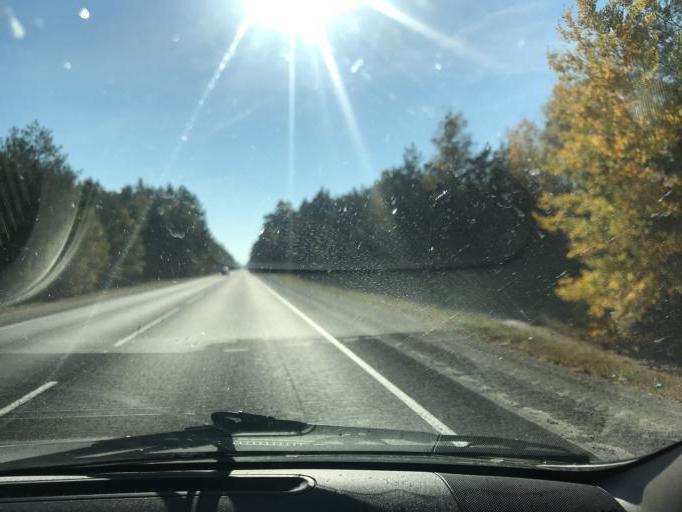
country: BY
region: Brest
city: Mikashevichy
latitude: 52.2758
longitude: 27.4414
